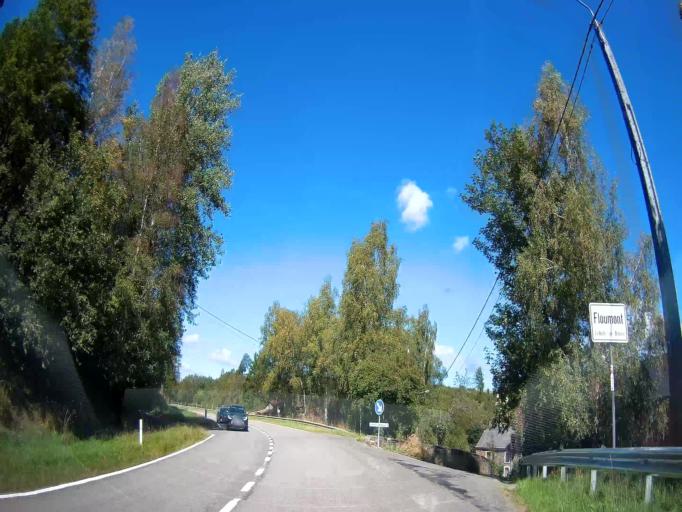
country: BE
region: Wallonia
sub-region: Province du Luxembourg
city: Bertogne
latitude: 50.1135
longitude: 5.6285
